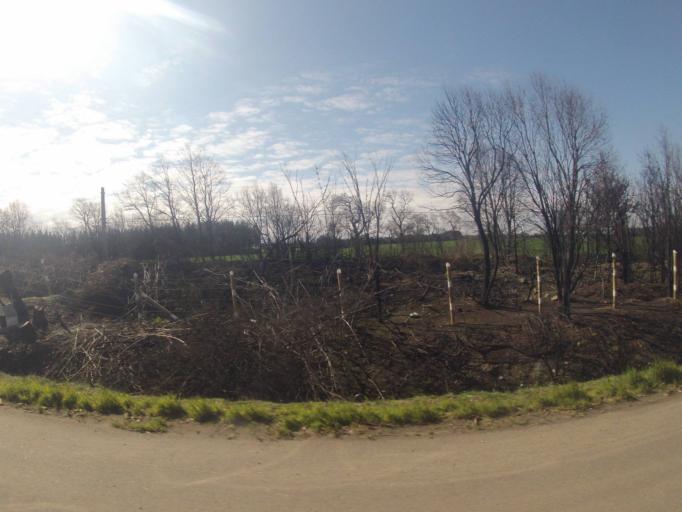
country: CL
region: Araucania
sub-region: Provincia de Malleco
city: Victoria
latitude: -38.1528
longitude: -72.3065
